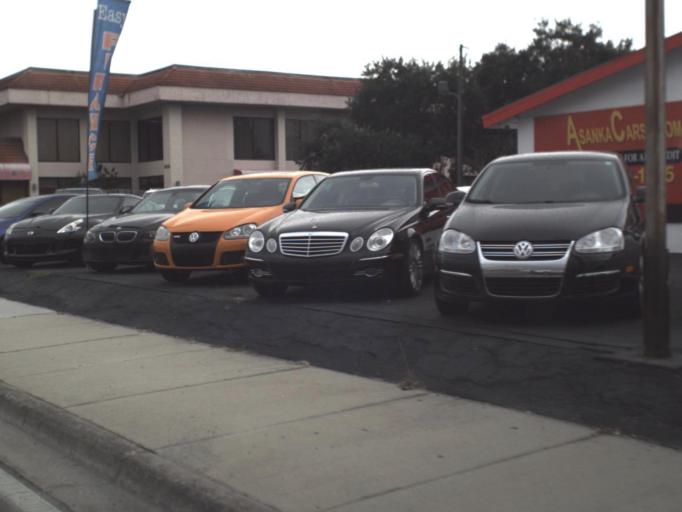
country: US
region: Florida
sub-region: Sarasota County
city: Southgate
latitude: 27.2987
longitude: -82.5135
